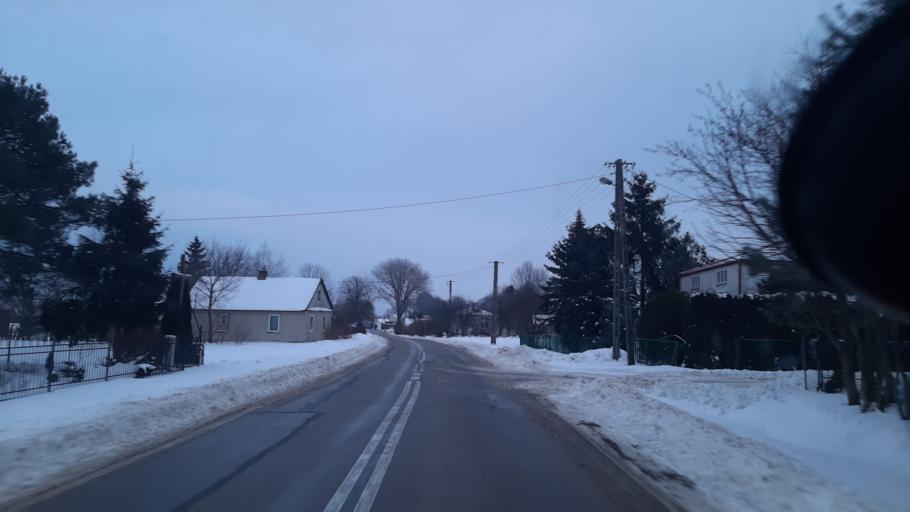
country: PL
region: Lublin Voivodeship
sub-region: Powiat lubelski
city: Jastkow
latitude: 51.3437
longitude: 22.4055
